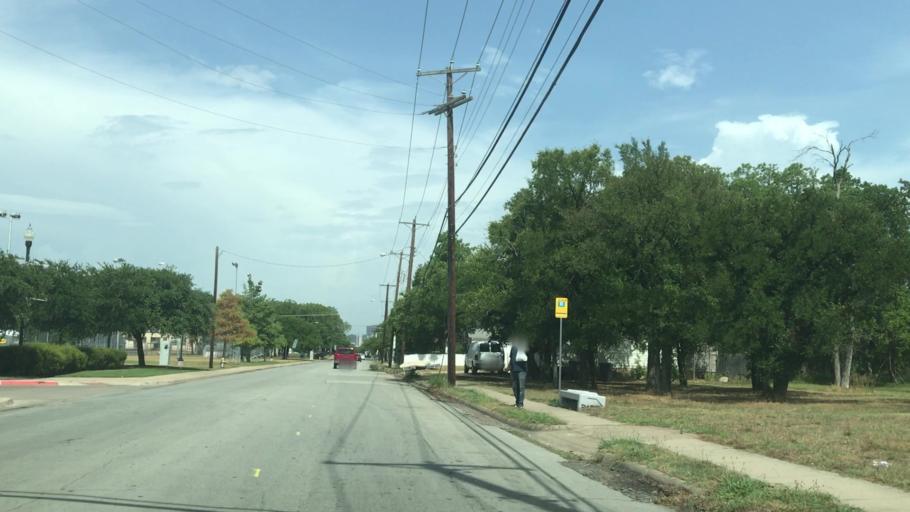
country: US
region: Texas
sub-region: Dallas County
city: Dallas
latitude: 32.7871
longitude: -96.8557
